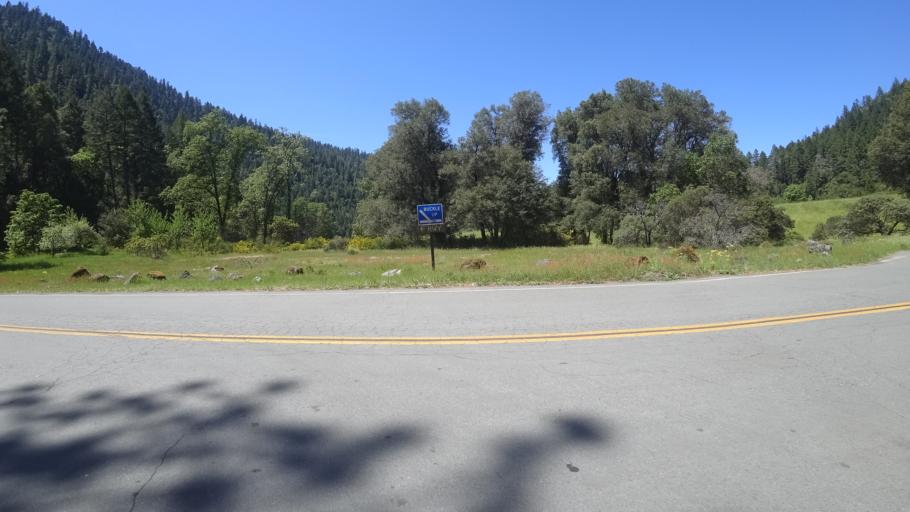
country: US
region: California
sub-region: Humboldt County
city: Willow Creek
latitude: 40.8825
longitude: -123.5475
